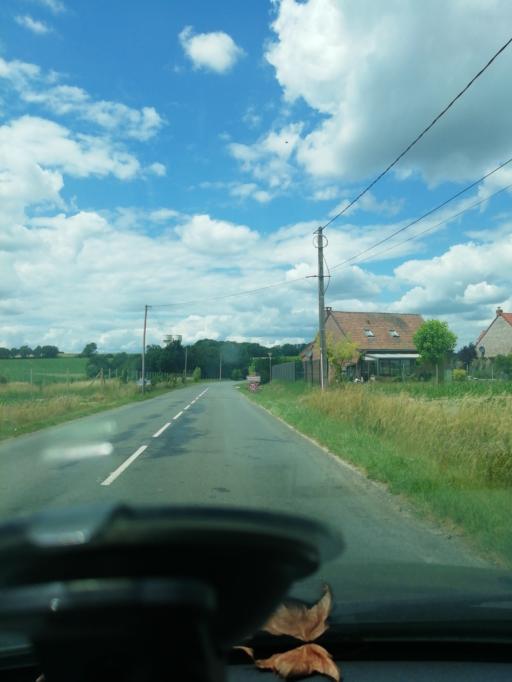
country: FR
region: Nord-Pas-de-Calais
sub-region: Departement du Nord
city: Lewarde
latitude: 50.3116
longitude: 3.1687
